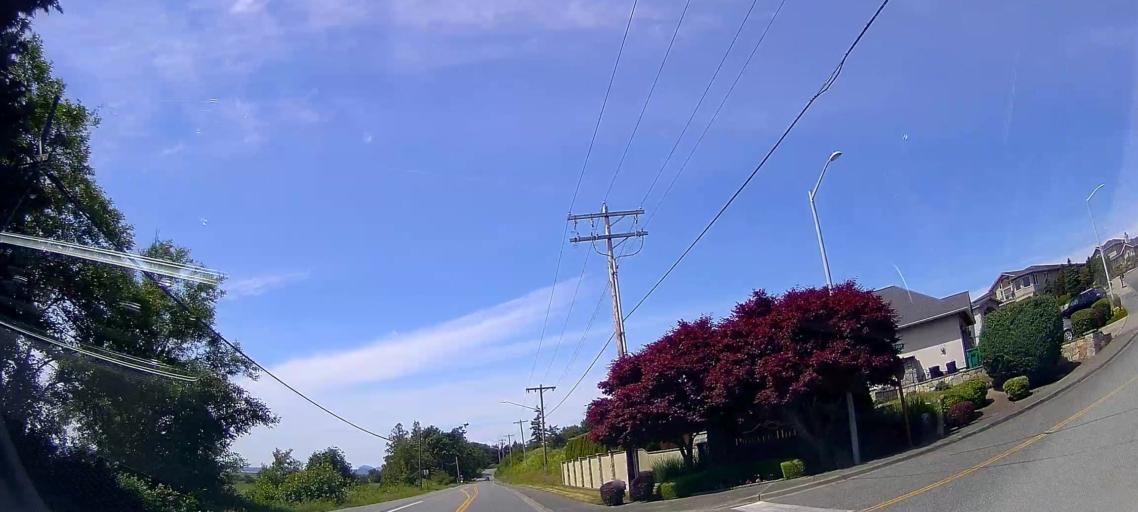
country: US
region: Washington
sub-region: Snohomish County
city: Stanwood
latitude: 48.2505
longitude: -122.3517
